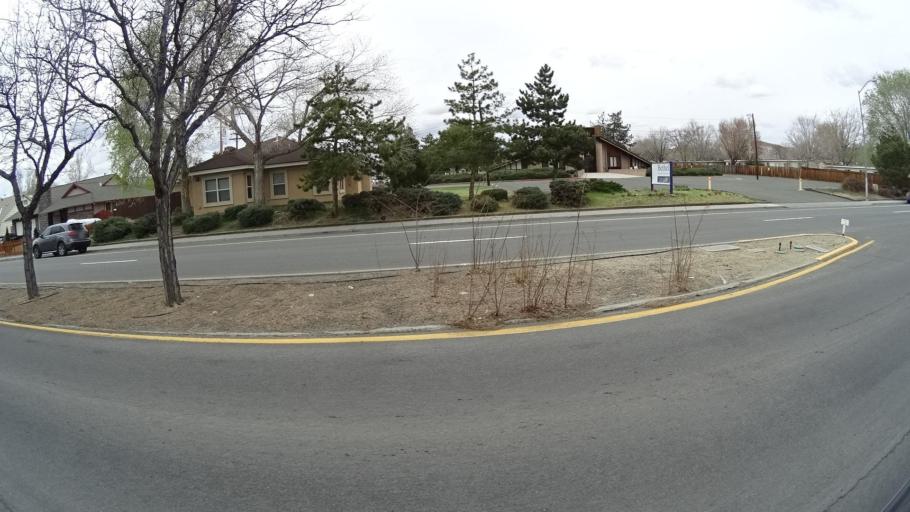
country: US
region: Nevada
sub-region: Washoe County
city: Sparks
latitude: 39.5549
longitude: -119.7618
